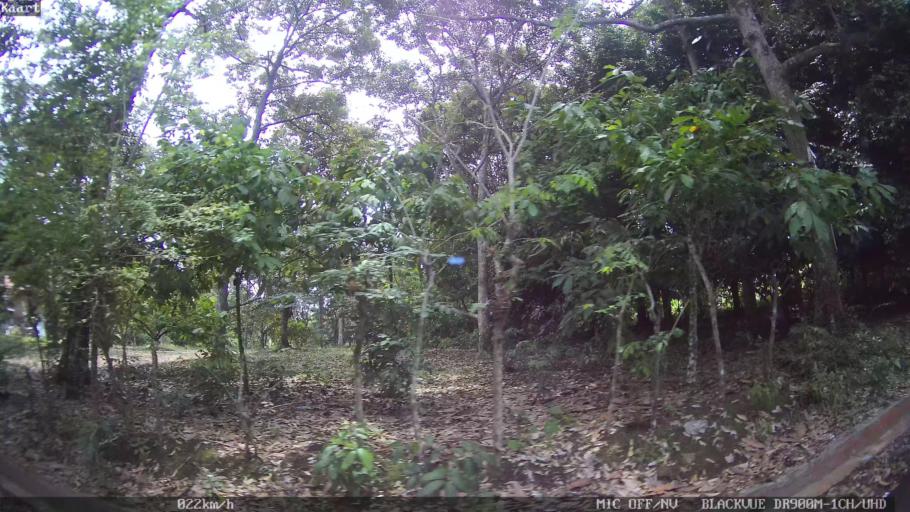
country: ID
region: Lampung
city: Bandarlampung
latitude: -5.4206
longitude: 105.2231
